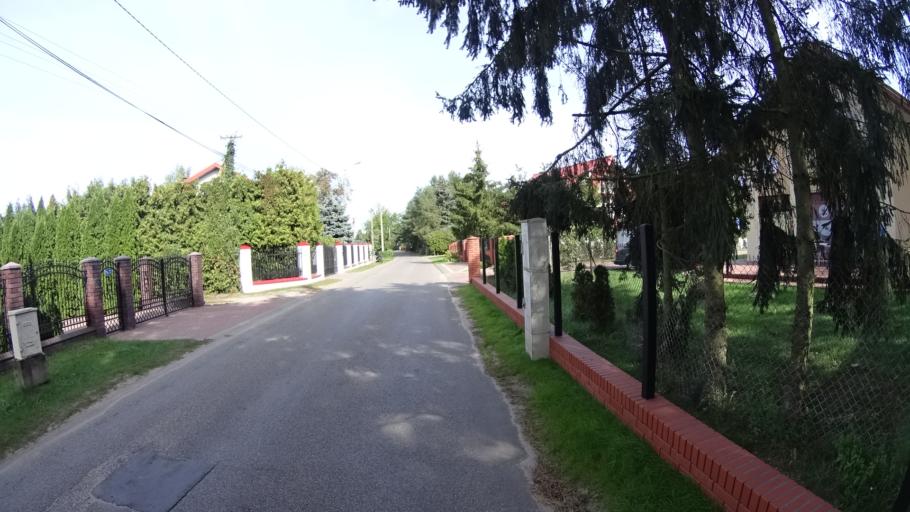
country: PL
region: Masovian Voivodeship
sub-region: Powiat legionowski
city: Serock
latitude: 52.4854
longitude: 21.0789
